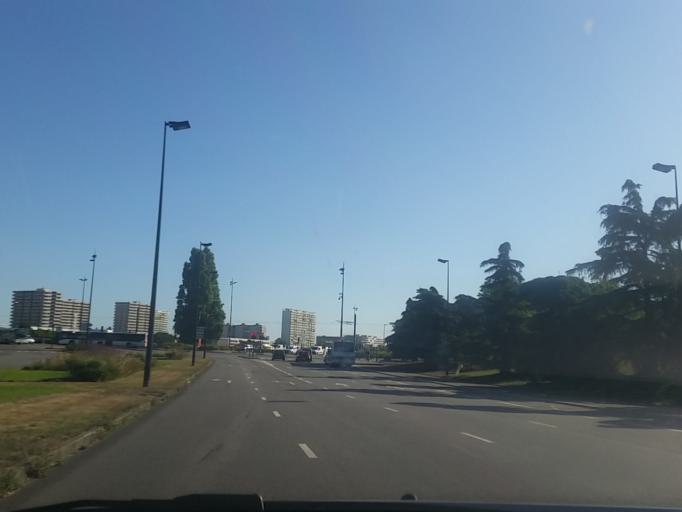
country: FR
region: Pays de la Loire
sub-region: Departement de la Loire-Atlantique
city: Reze
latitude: 47.1968
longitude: -1.5431
